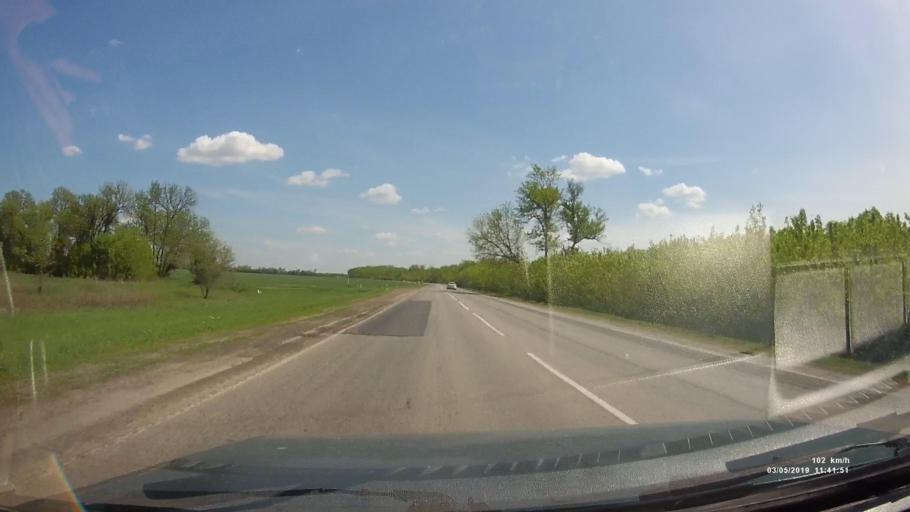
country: RU
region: Rostov
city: Ol'ginskaya
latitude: 47.1365
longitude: 40.0319
